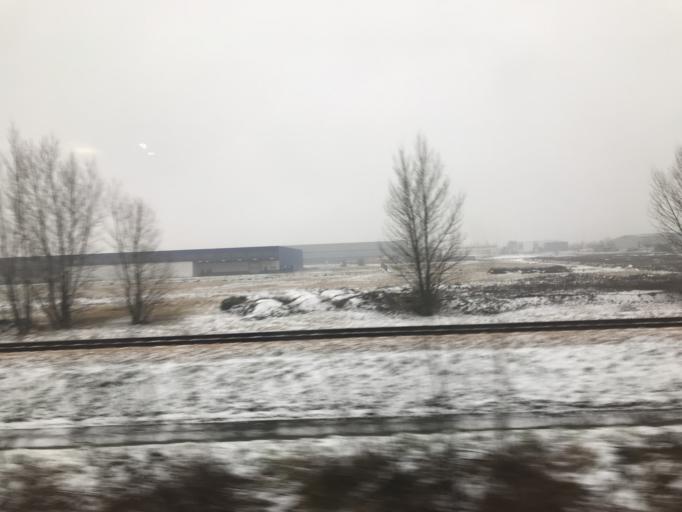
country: HU
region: Gyor-Moson-Sopron
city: Toltestava
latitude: 47.6837
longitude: 17.7065
